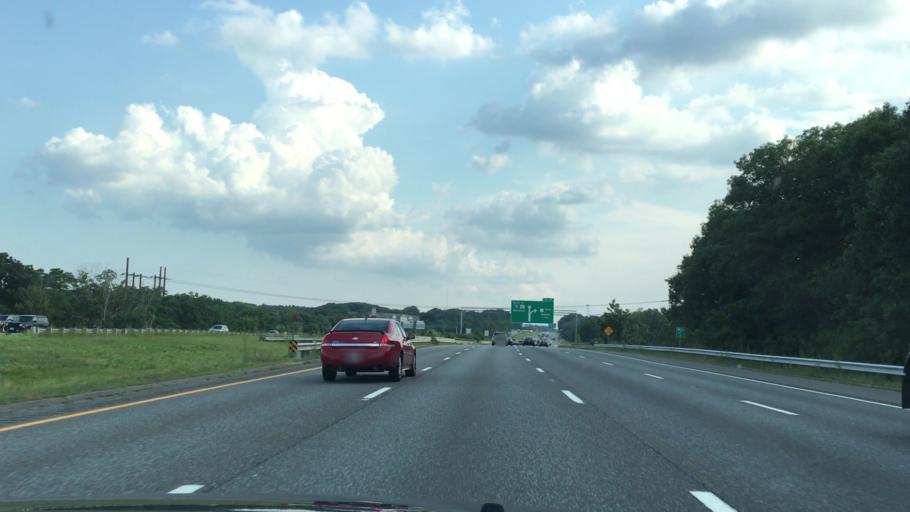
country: US
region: Massachusetts
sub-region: Essex County
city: Danvers
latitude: 42.5609
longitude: -70.9738
